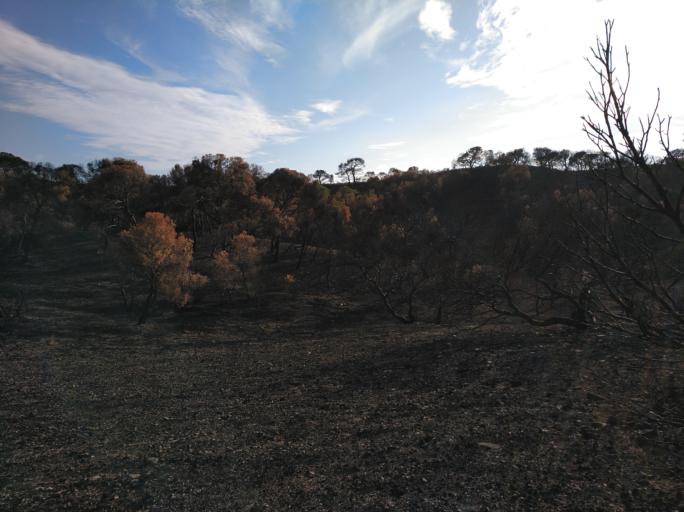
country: ES
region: Aragon
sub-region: Provincia de Zaragoza
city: San Mateo de Gallego
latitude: 41.7596
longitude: -0.7310
